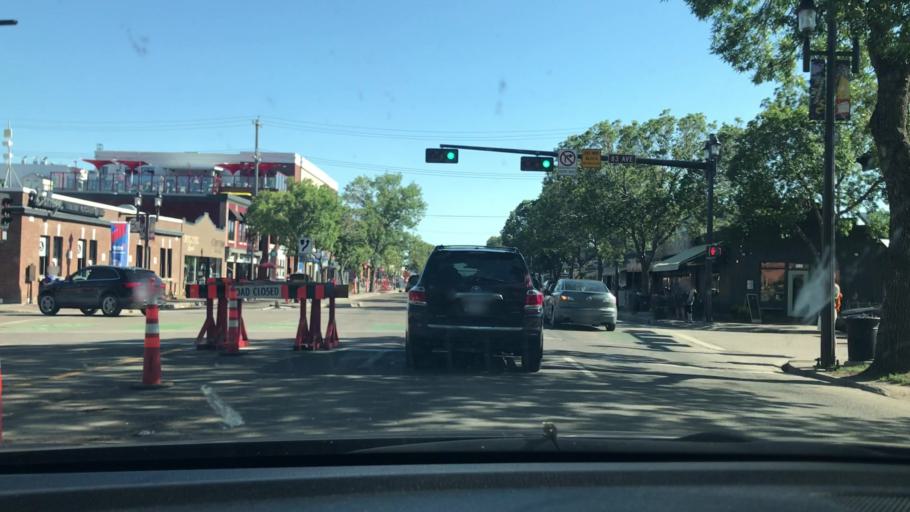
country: CA
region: Alberta
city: Edmonton
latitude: 53.5193
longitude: -113.4976
